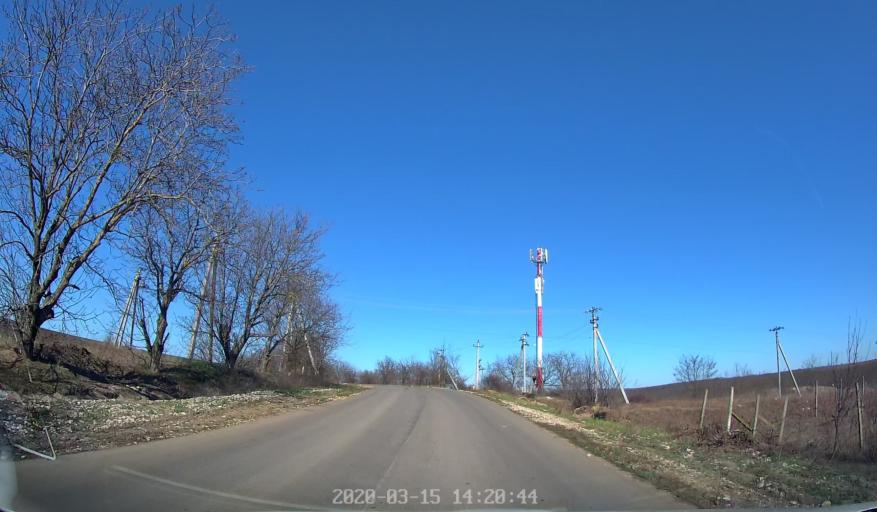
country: MD
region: Orhei
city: Orhei
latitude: 47.3120
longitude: 28.9240
